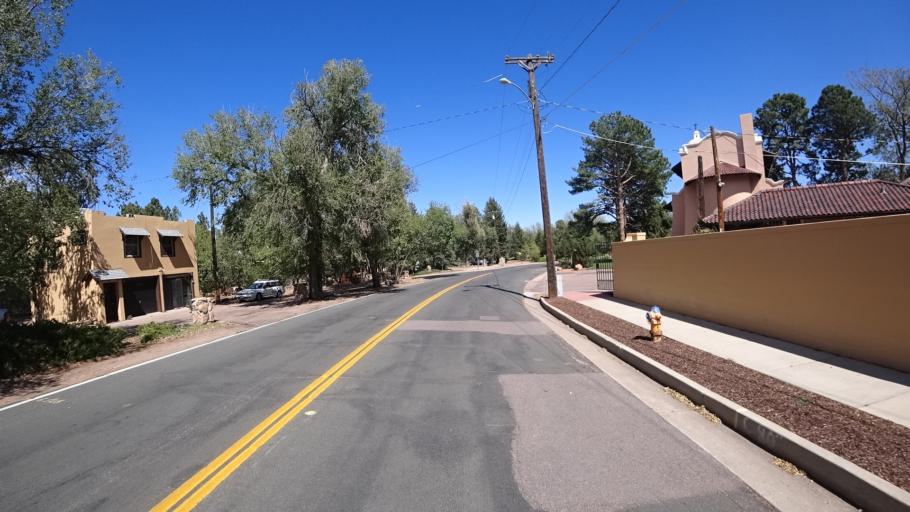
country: US
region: Colorado
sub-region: El Paso County
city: Colorado Springs
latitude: 38.7919
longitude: -104.8549
